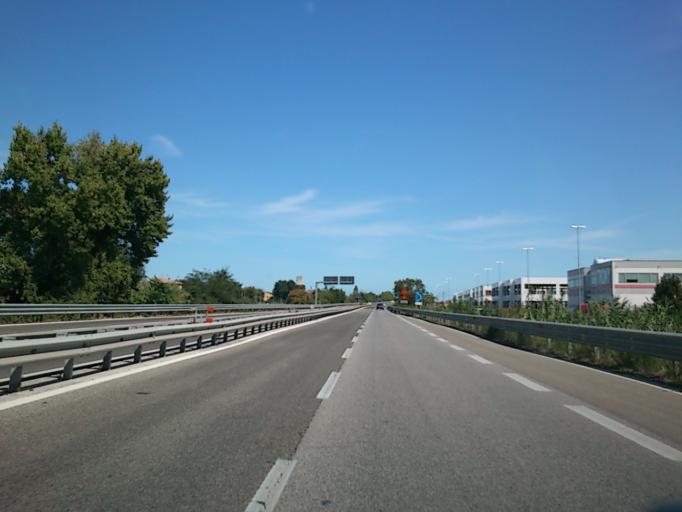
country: IT
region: The Marches
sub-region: Provincia di Pesaro e Urbino
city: Bellocchi
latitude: 43.7893
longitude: 12.9966
